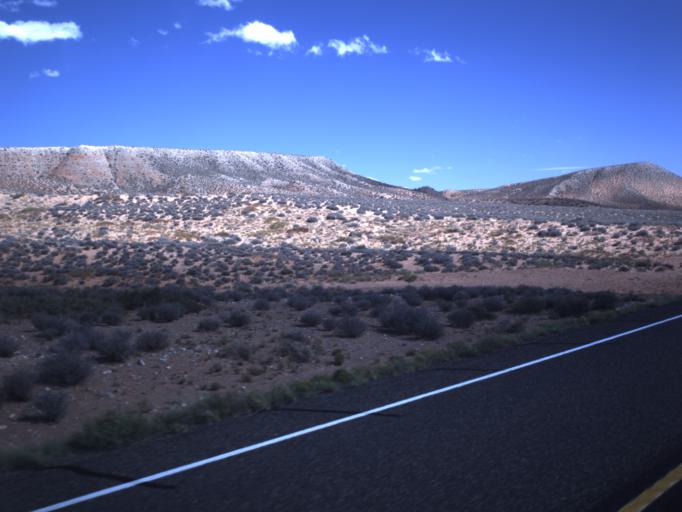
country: US
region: Utah
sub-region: Wayne County
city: Loa
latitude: 38.0844
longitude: -110.6145
